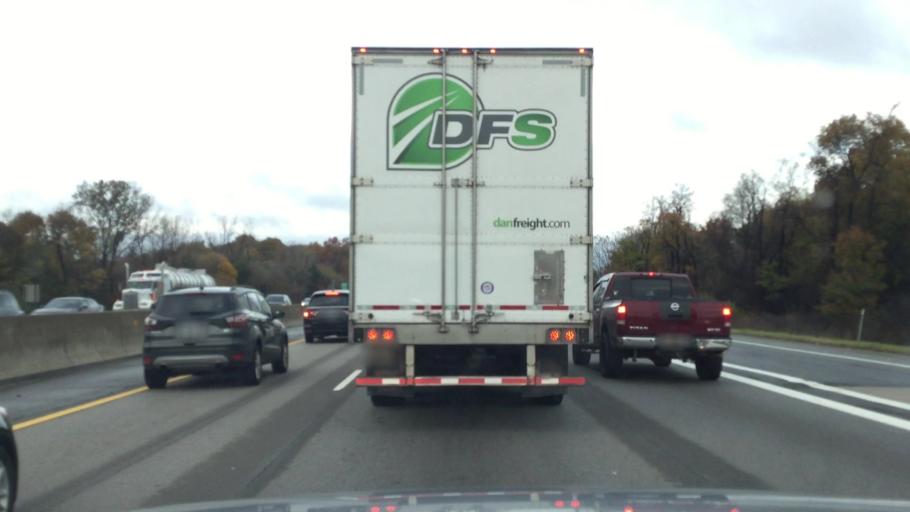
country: US
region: Michigan
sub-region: Washtenaw County
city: Ypsilanti
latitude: 42.2245
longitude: -83.6570
